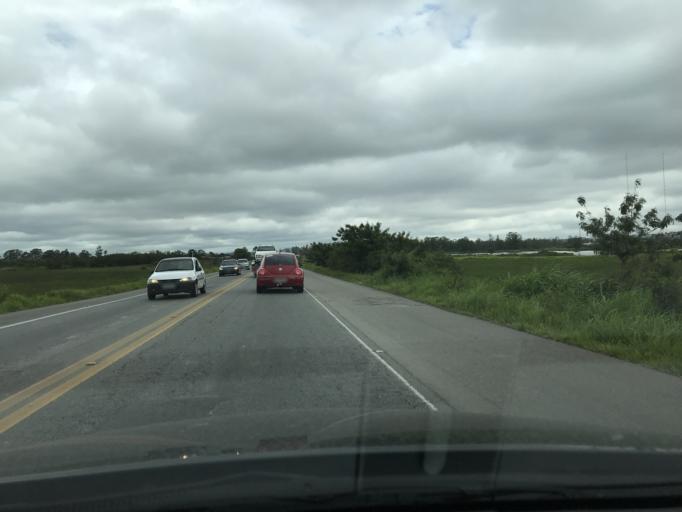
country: BR
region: Sao Paulo
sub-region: Itaquaquecetuba
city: Itaquaquecetuba
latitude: -23.4815
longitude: -46.3261
